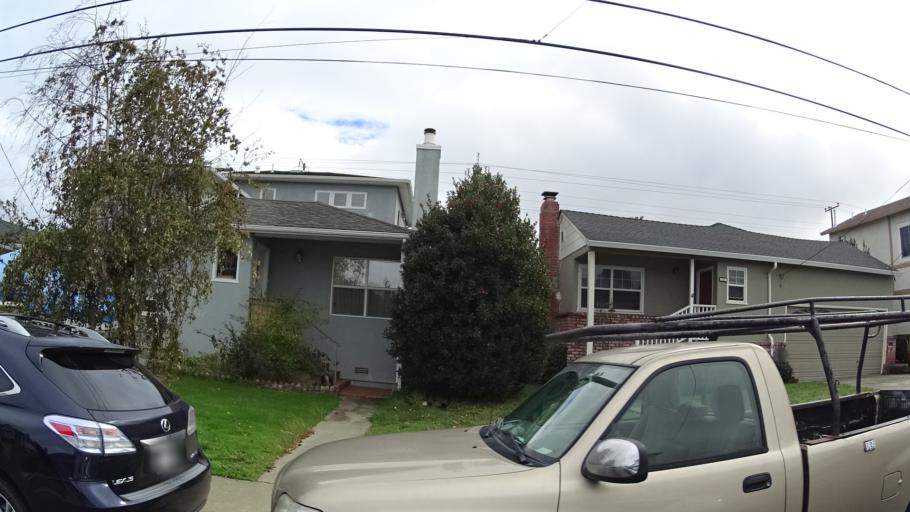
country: US
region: California
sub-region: San Mateo County
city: Millbrae
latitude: 37.6009
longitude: -122.4035
